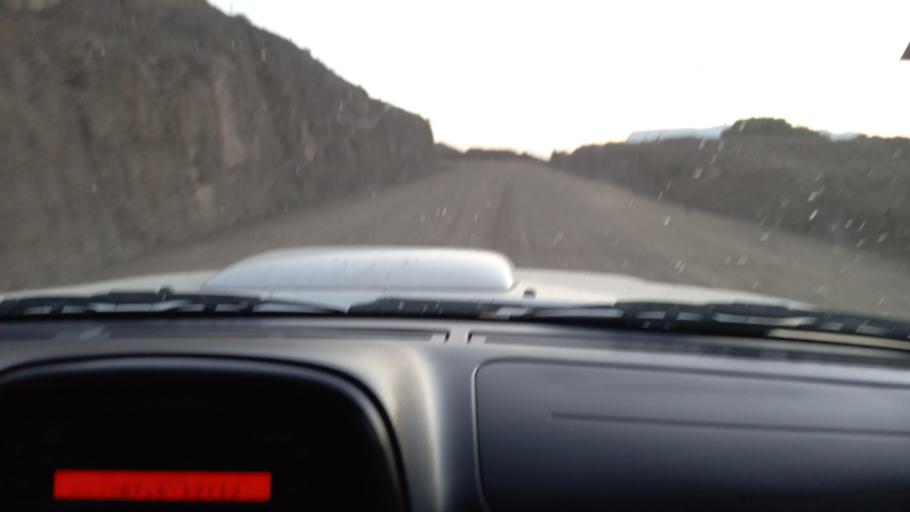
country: ET
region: Amhara
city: Debark'
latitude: 13.0375
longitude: 38.0562
